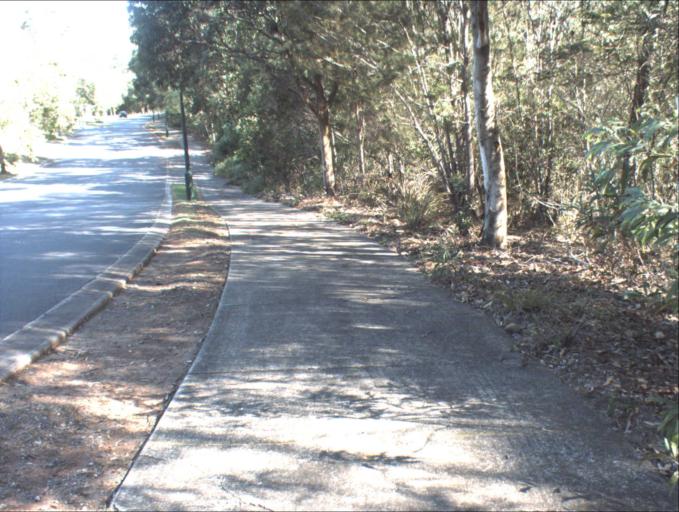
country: AU
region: Queensland
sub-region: Logan
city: Slacks Creek
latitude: -27.6307
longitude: 153.1579
